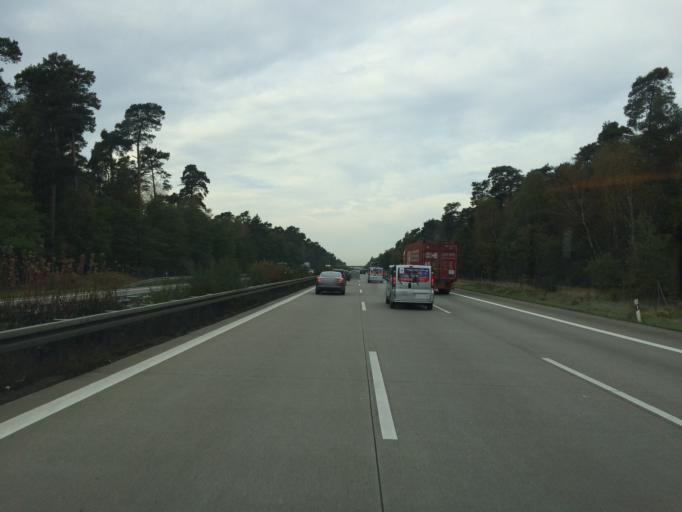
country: DE
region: Saxony-Anhalt
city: Tucheim
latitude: 52.2397
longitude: 12.1114
